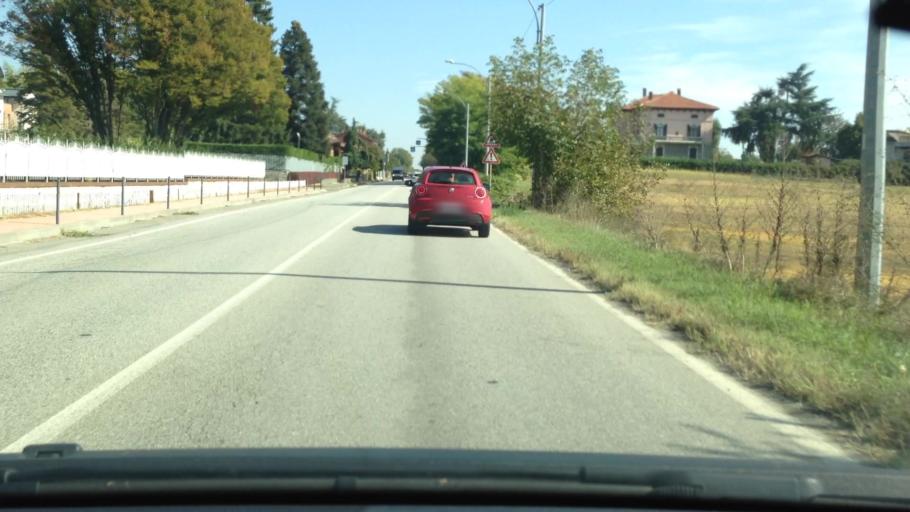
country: IT
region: Piedmont
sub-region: Provincia di Alessandria
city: Quattordio
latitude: 44.8986
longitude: 8.4115
